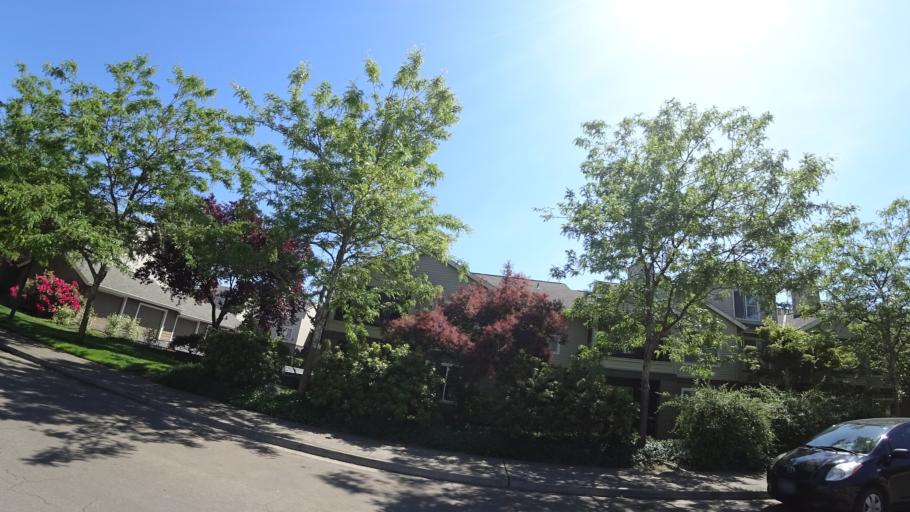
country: US
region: Oregon
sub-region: Washington County
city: King City
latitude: 45.4406
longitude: -122.8139
